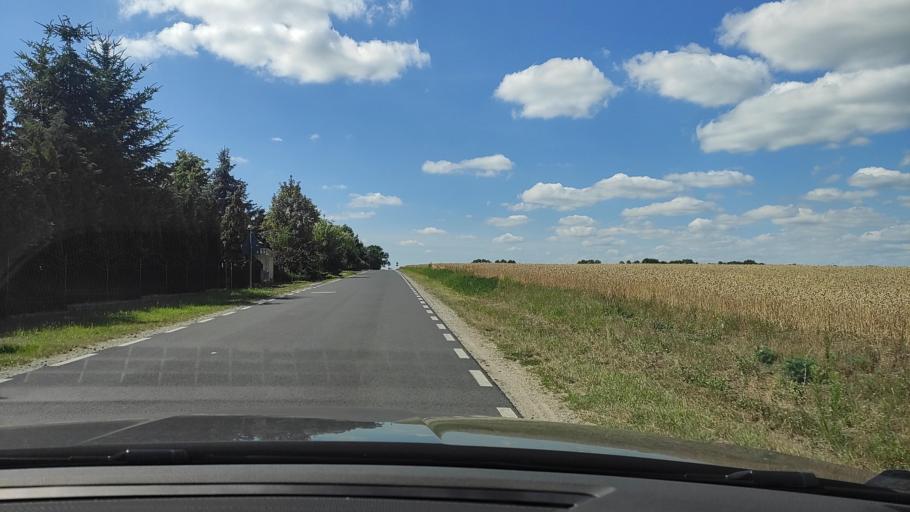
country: PL
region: Greater Poland Voivodeship
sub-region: Powiat poznanski
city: Kostrzyn
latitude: 52.4800
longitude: 17.1765
